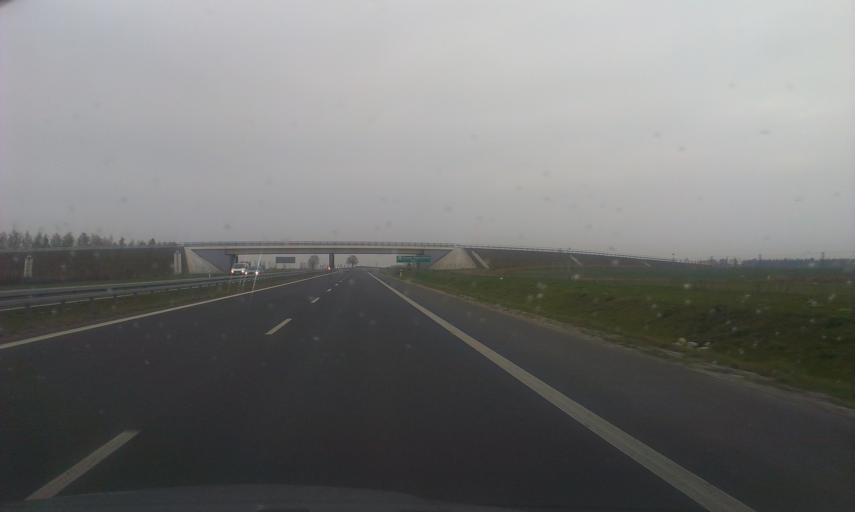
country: PL
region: Greater Poland Voivodeship
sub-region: Powiat poznanski
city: Rokietnica
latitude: 52.4593
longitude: 16.7343
